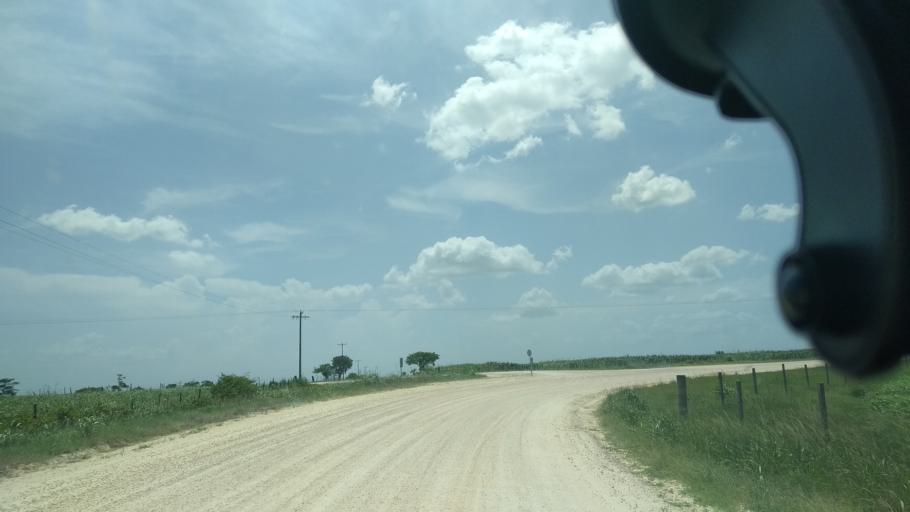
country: BZ
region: Cayo
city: San Ignacio
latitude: 17.3148
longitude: -89.0469
